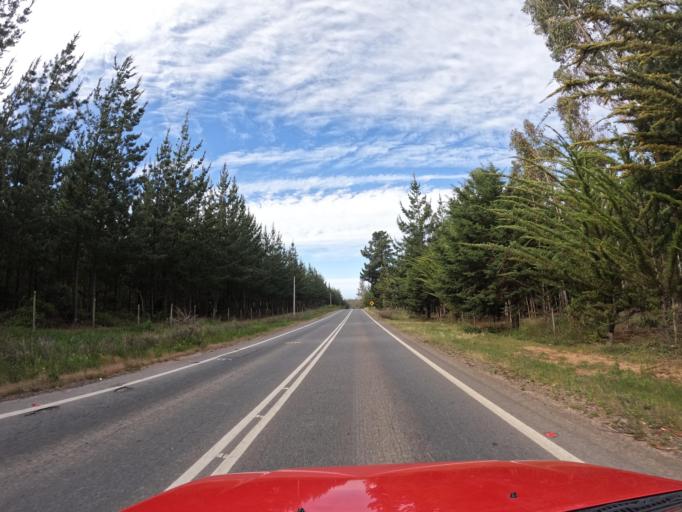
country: CL
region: O'Higgins
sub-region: Provincia de Colchagua
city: Santa Cruz
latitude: -34.3200
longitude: -71.8669
